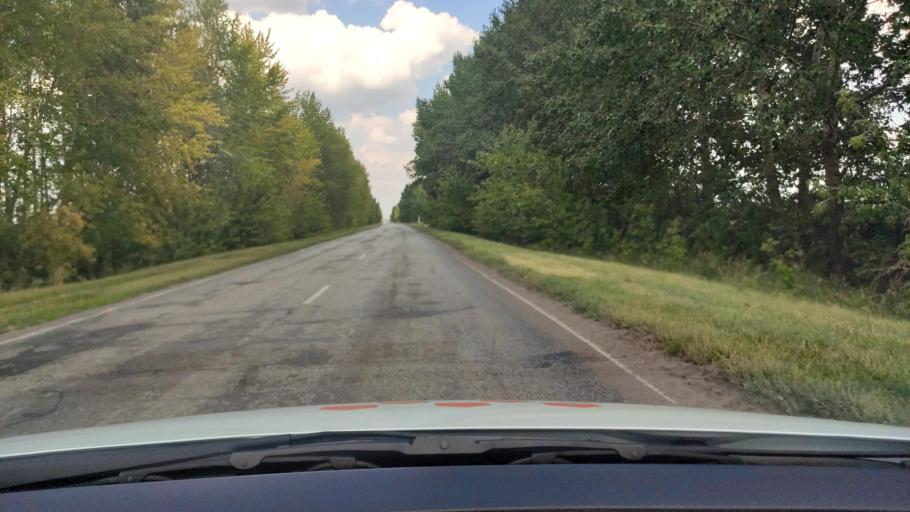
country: RU
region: Voronezj
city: Pereleshinskiy
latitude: 51.7278
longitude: 40.3742
